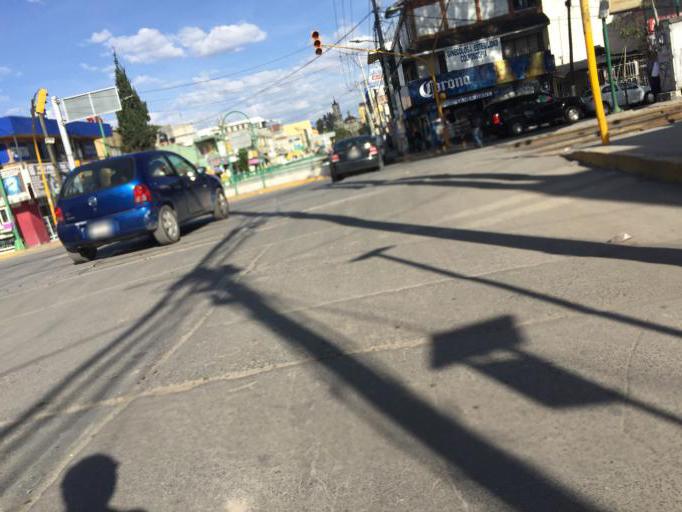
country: MX
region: Mexico
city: Cuautitlan
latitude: 19.6698
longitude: -99.1841
